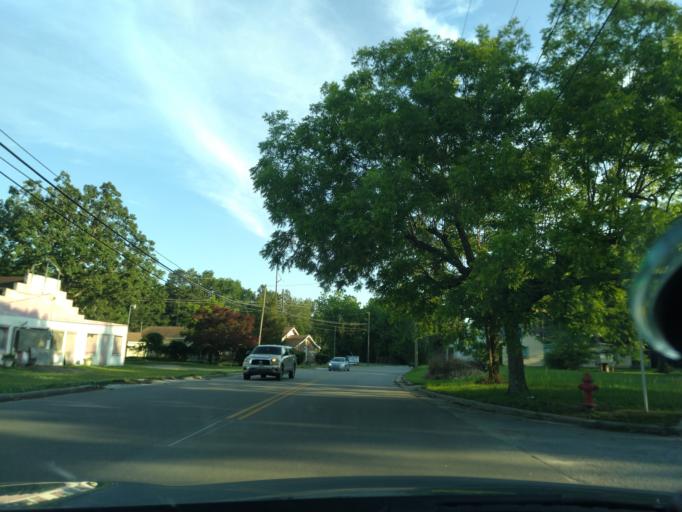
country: US
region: North Carolina
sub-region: Washington County
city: Plymouth
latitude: 35.8577
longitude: -76.7542
